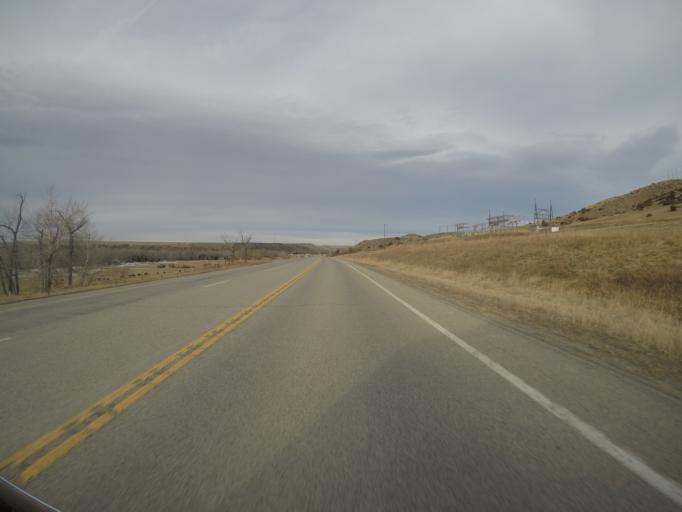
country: US
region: Montana
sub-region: Stillwater County
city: Absarokee
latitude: 45.4986
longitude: -109.4490
